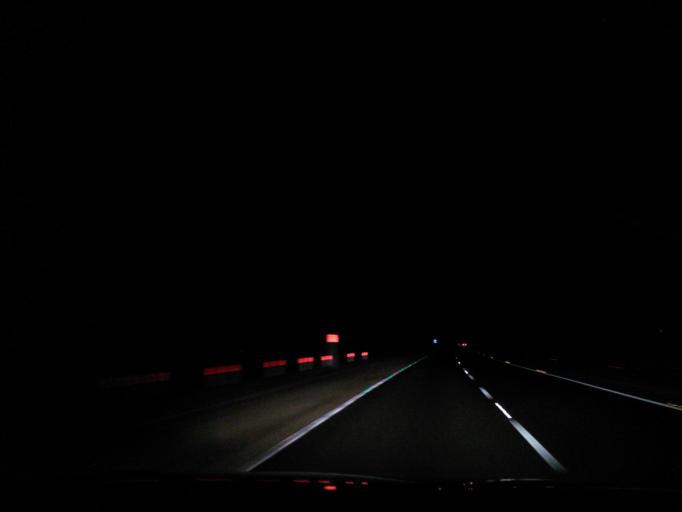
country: GB
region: England
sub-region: North Yorkshire
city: Thirsk
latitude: 54.2153
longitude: -1.3408
